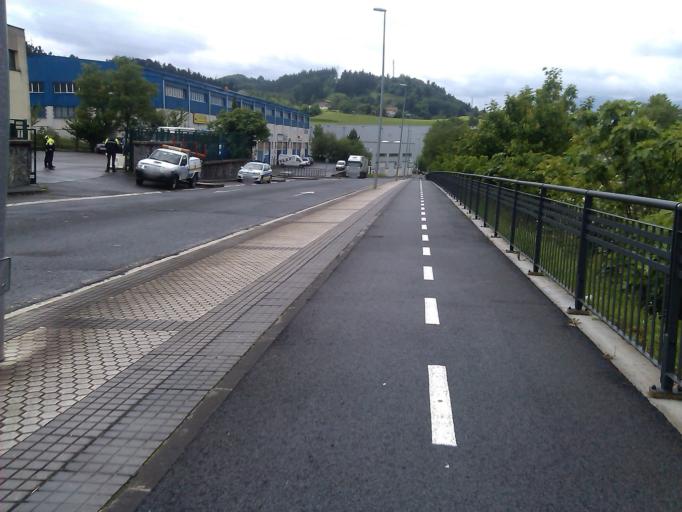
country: ES
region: Basque Country
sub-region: Provincia de Guipuzcoa
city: Urnieta
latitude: 43.2284
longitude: -2.0042
